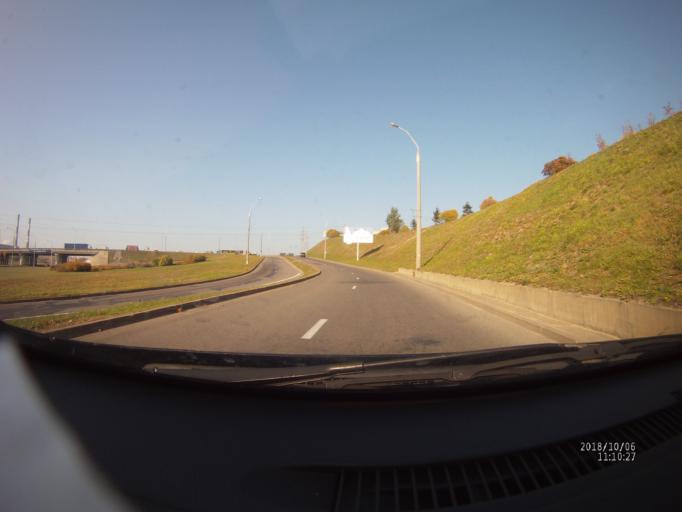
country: BY
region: Minsk
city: Malinovka
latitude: 53.8804
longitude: 27.4202
